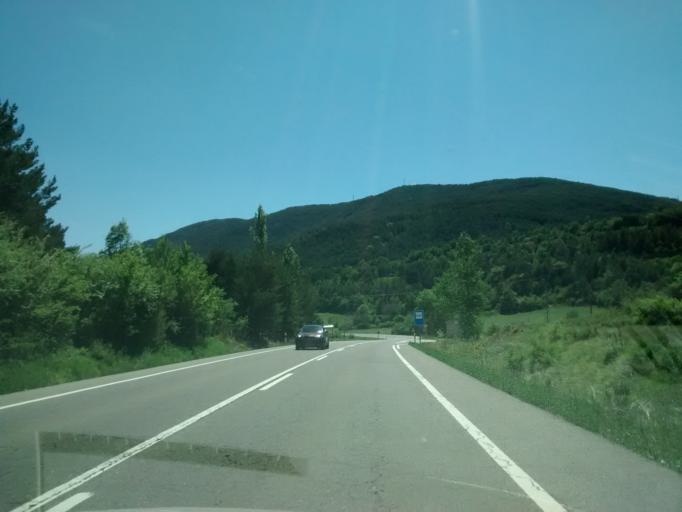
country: ES
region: Aragon
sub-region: Provincia de Huesca
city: Castiello de Jaca
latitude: 42.6565
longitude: -0.5567
